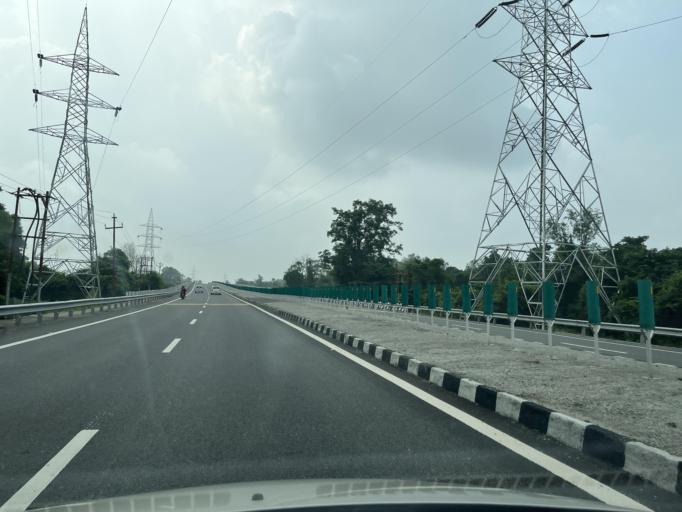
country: IN
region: Uttarakhand
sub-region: Dehradun
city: Raiwala
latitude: 30.1044
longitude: 78.1751
